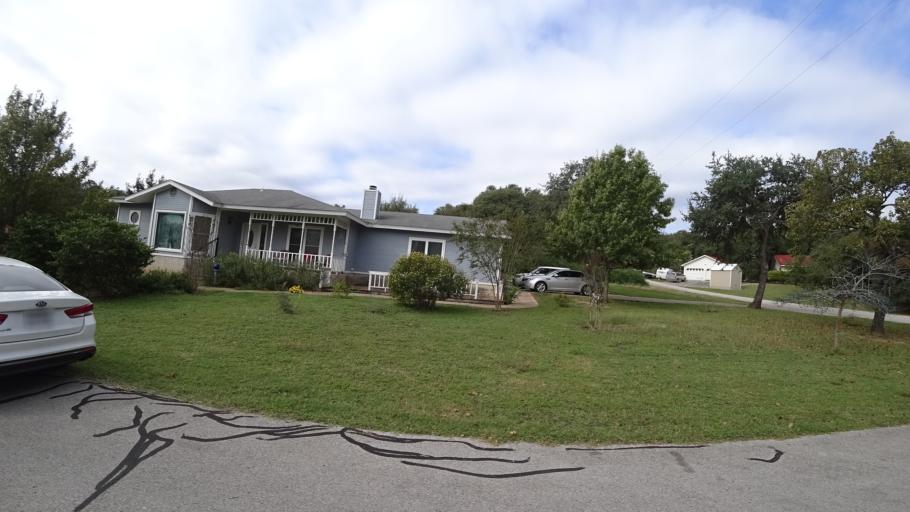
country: US
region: Texas
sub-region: Travis County
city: Shady Hollow
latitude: 30.1331
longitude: -97.8872
